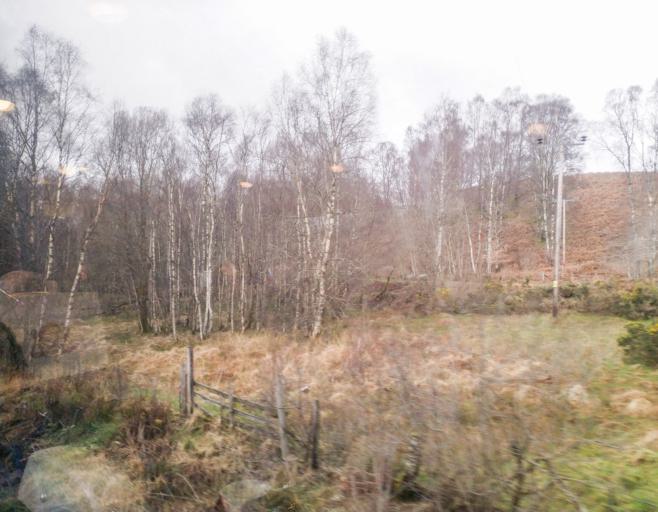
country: GB
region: Scotland
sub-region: Highland
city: Spean Bridge
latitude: 56.8870
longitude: -4.8259
